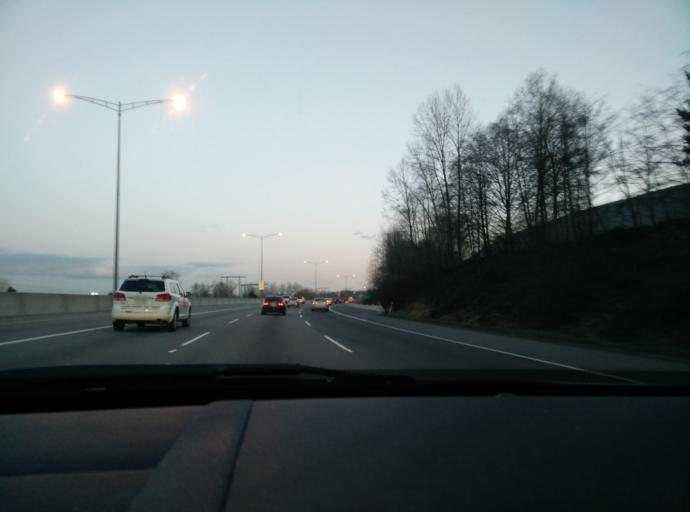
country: CA
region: British Columbia
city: Burnaby
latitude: 49.2561
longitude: -122.9796
